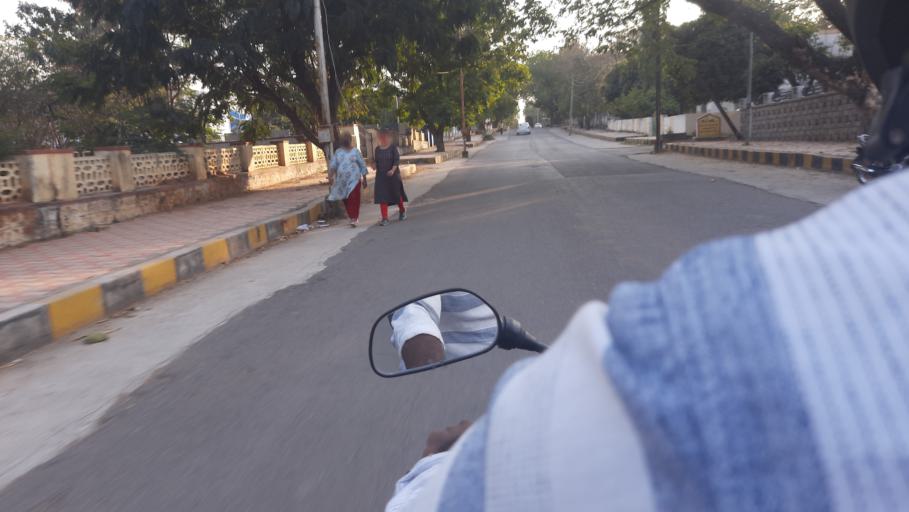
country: IN
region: Telangana
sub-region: Rangareddi
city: Secunderabad
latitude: 17.4879
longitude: 78.5487
